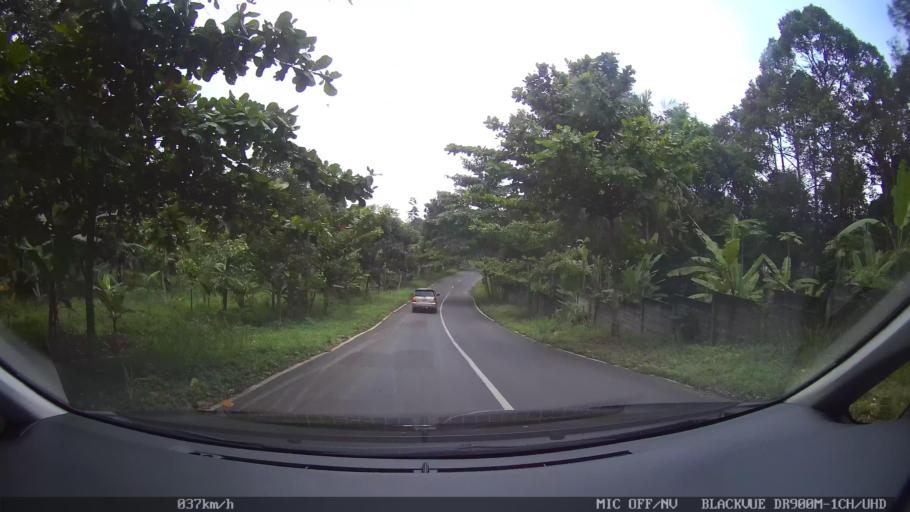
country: ID
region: Lampung
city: Bandarlampung
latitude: -5.4365
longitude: 105.2187
